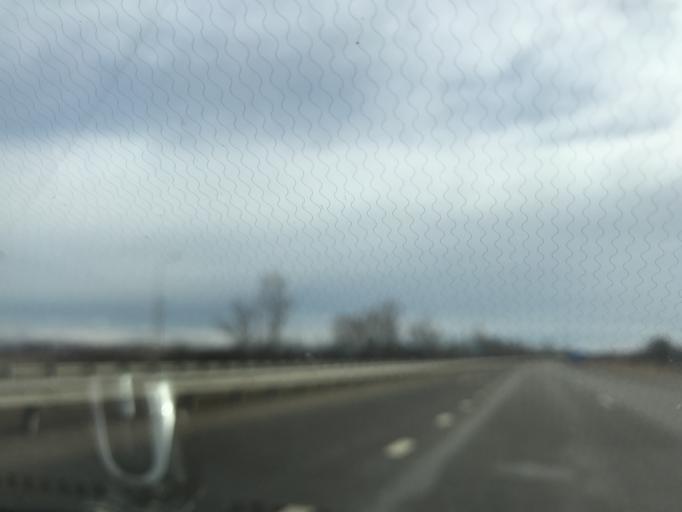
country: RU
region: Stavropol'skiy
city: Barsukovskaya
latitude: 44.7129
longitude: 41.8464
